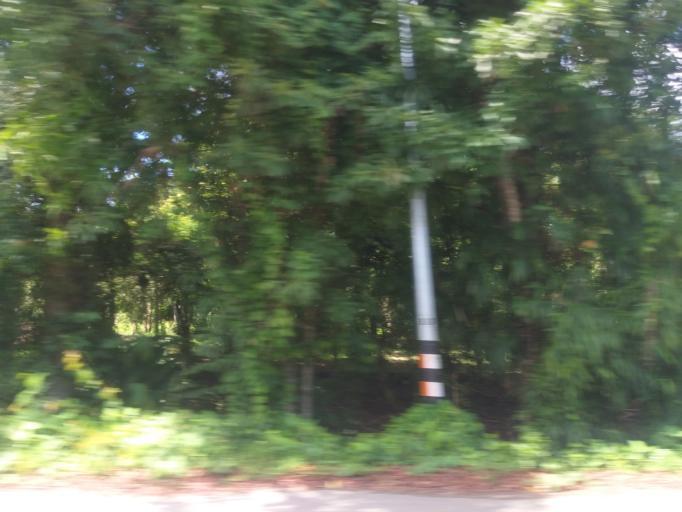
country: TH
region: Nakhon Nayok
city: Nakhon Nayok
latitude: 14.2748
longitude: 101.2788
